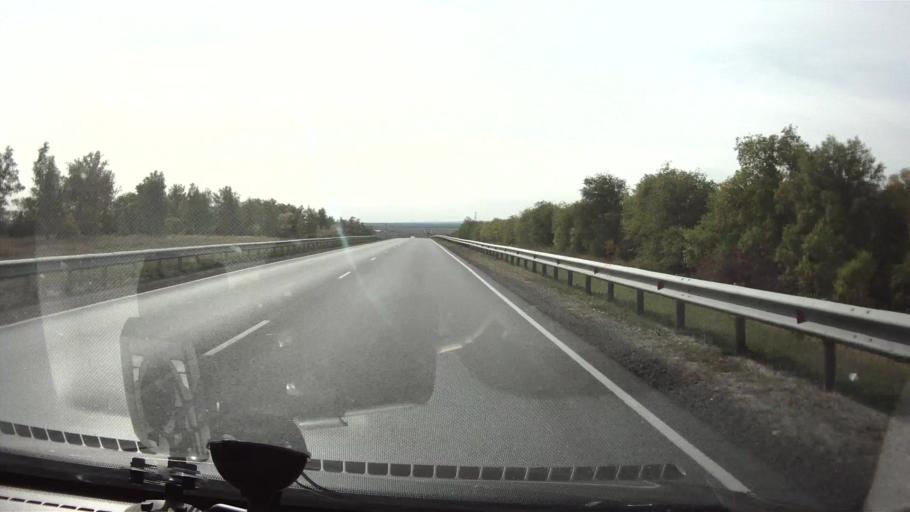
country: RU
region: Saratov
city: Balakovo
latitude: 52.0884
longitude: 47.6863
